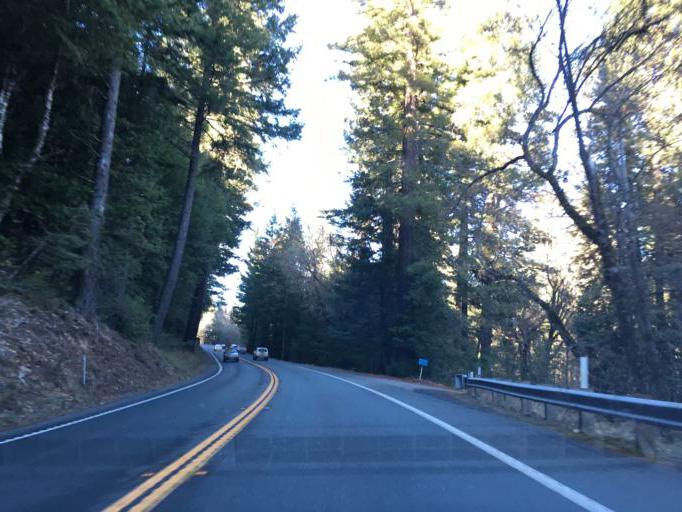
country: US
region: California
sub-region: Mendocino County
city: Brooktrails
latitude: 39.4859
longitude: -123.3606
